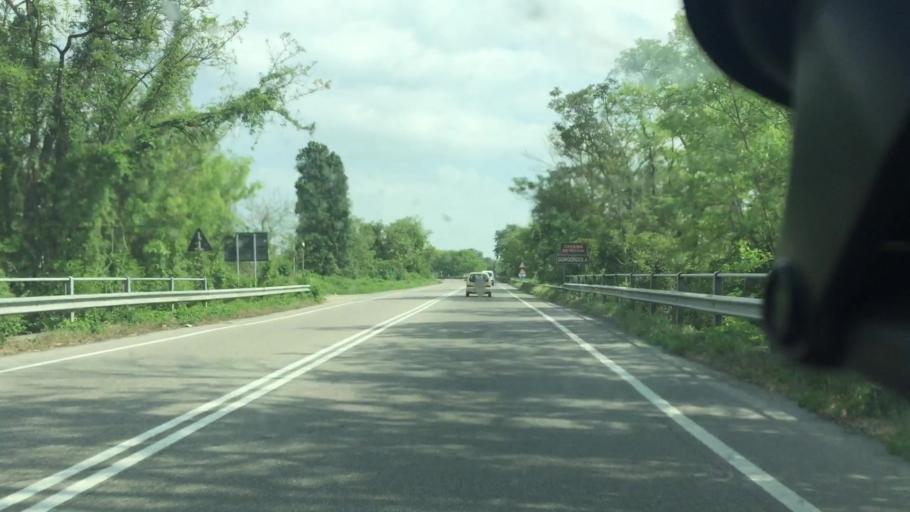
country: IT
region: Lombardy
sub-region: Citta metropolitana di Milano
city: Sant'Agata Martesana
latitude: 45.5229
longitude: 9.3947
